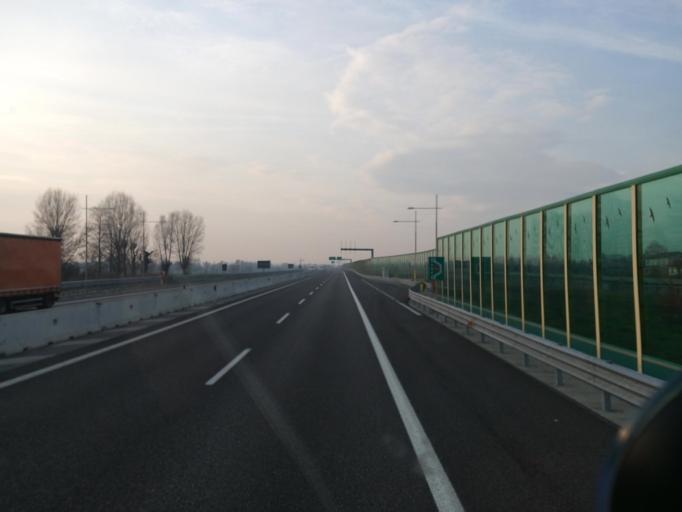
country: IT
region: Lombardy
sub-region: Provincia di Brescia
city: Flero
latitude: 45.4766
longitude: 10.1696
